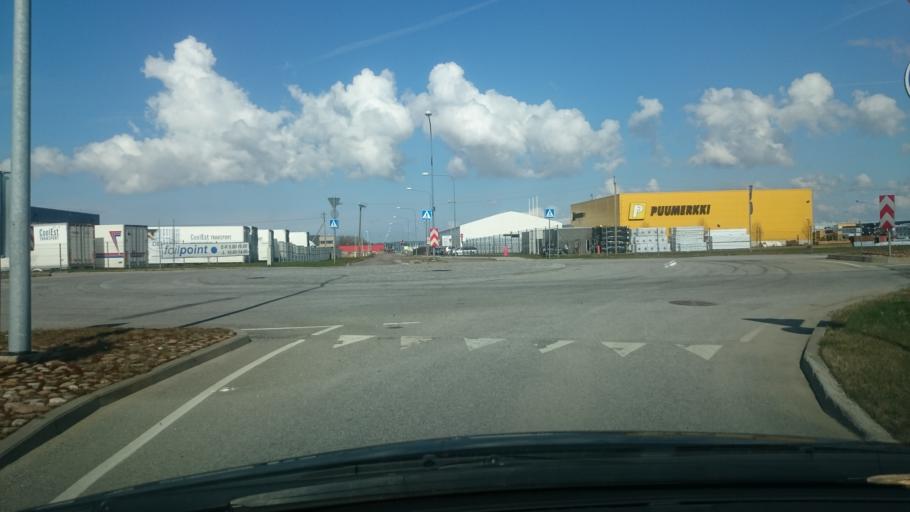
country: EE
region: Harju
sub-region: Rae vald
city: Jueri
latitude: 59.3660
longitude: 24.8711
